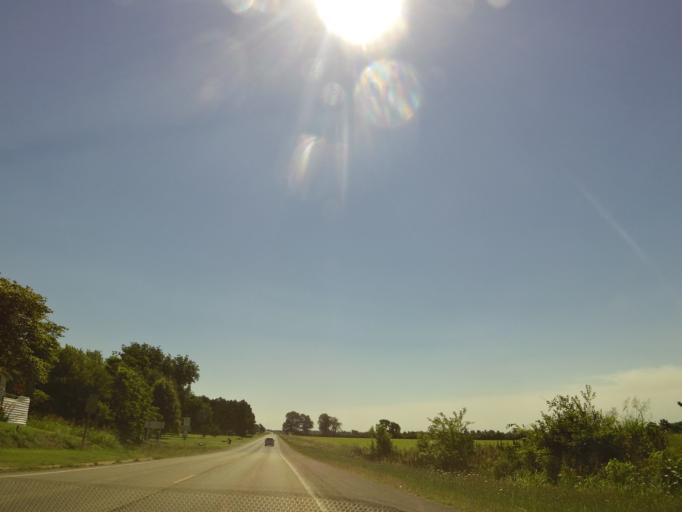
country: US
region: Missouri
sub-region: Dunklin County
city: Campbell
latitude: 36.4921
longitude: -90.0631
